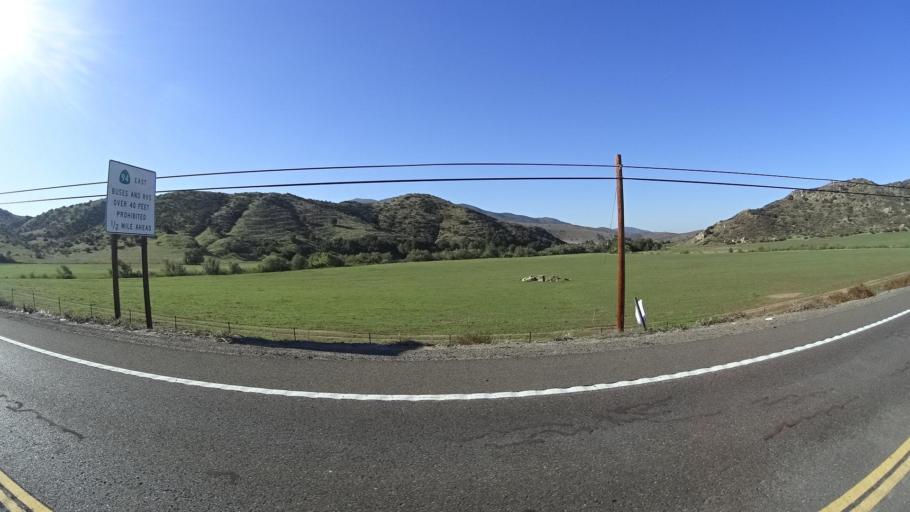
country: US
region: California
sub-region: San Diego County
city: Jamul
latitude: 32.6708
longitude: -116.8310
